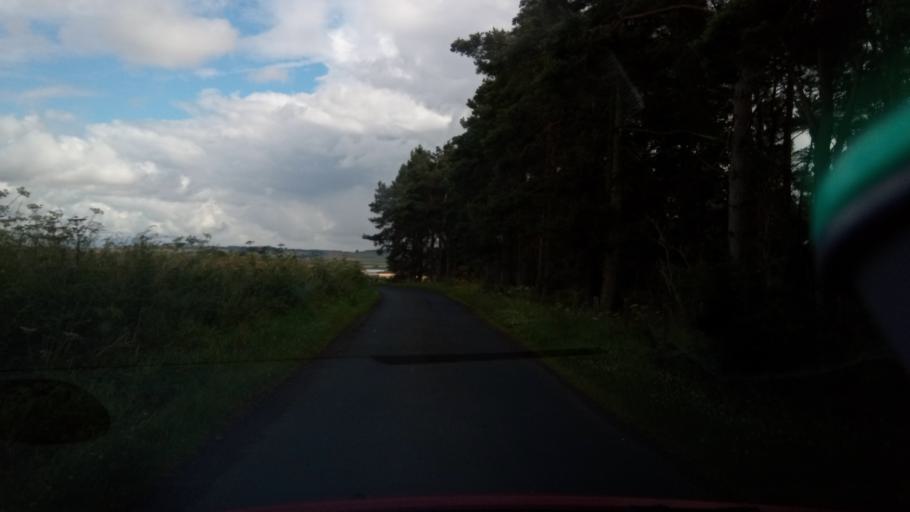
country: GB
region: Scotland
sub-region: The Scottish Borders
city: Kelso
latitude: 55.5138
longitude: -2.4154
